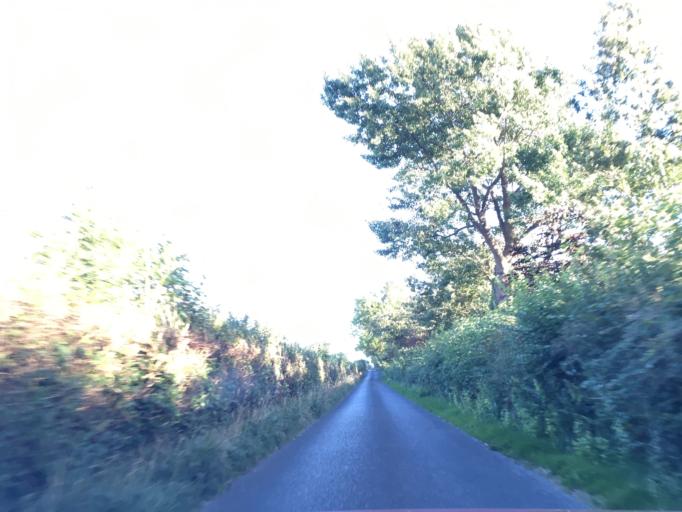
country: IE
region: Munster
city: Cashel
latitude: 52.5068
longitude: -7.9334
